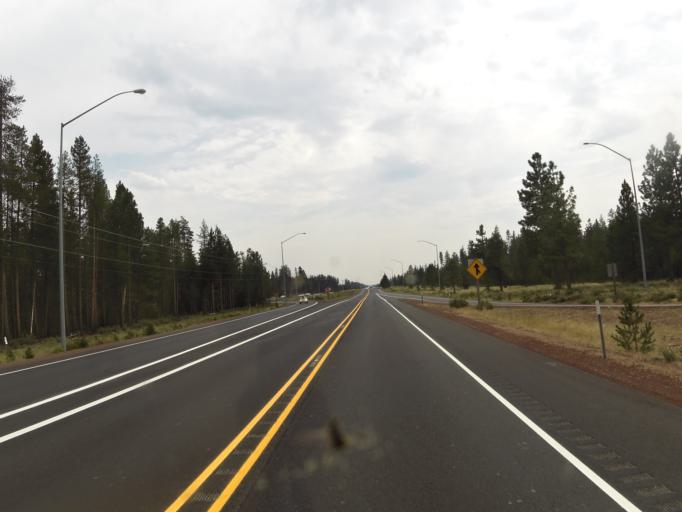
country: US
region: Oregon
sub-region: Deschutes County
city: La Pine
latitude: 43.1744
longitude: -121.7861
